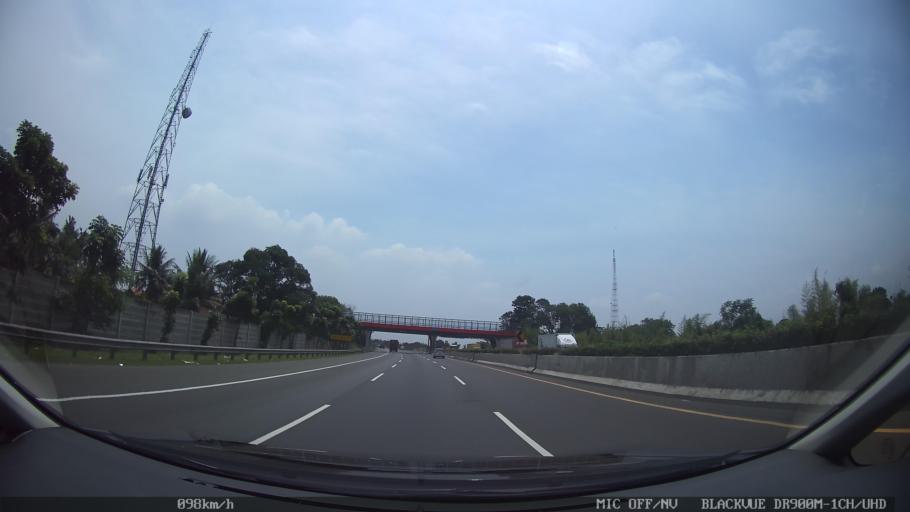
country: ID
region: West Java
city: Kresek
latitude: -6.1781
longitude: 106.3877
